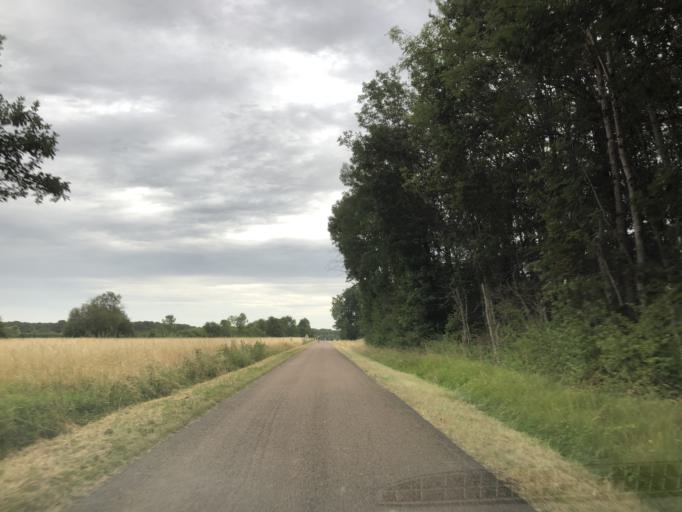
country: FR
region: Bourgogne
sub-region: Departement de l'Yonne
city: Aillant-sur-Tholon
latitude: 47.9006
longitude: 3.3010
